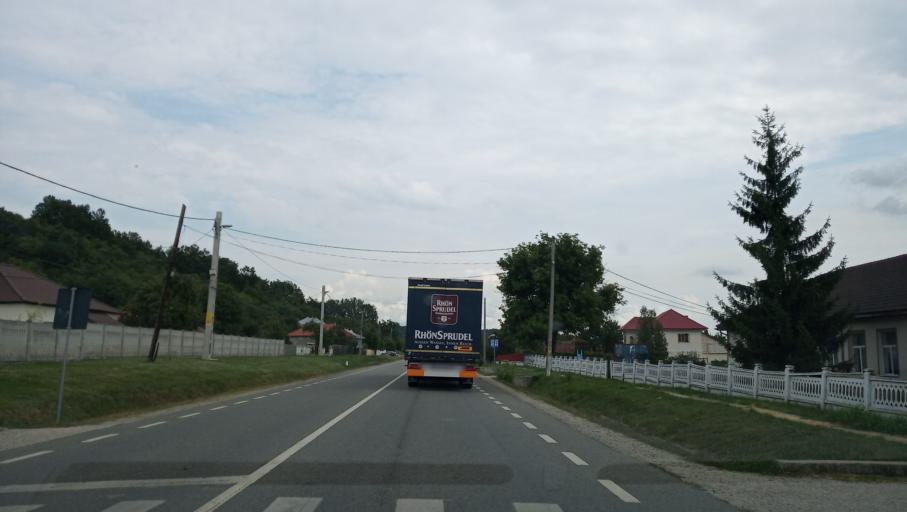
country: RO
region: Gorj
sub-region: Comuna Turceni
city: Turceni
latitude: 44.7123
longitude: 23.4006
